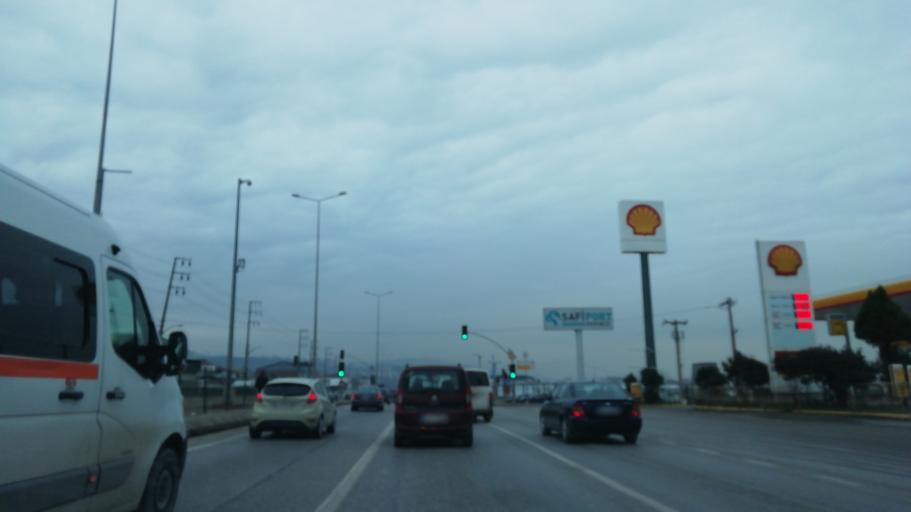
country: TR
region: Kocaeli
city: Derince
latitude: 40.7578
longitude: 29.8401
